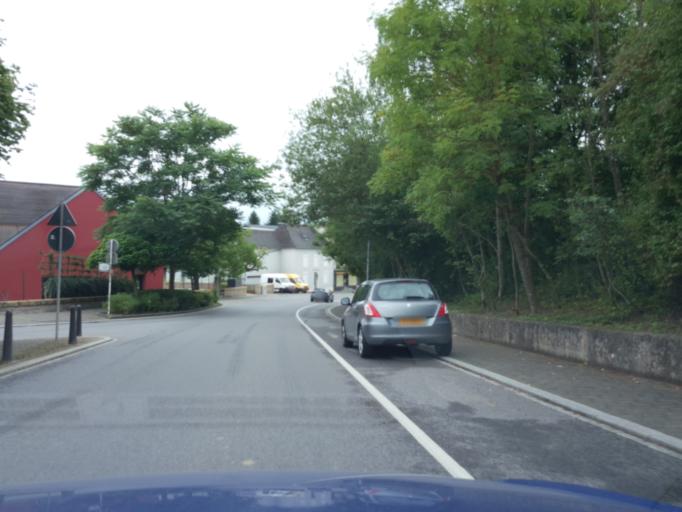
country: LU
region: Luxembourg
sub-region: Canton de Capellen
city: Mamer
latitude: 49.6315
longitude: 6.0206
